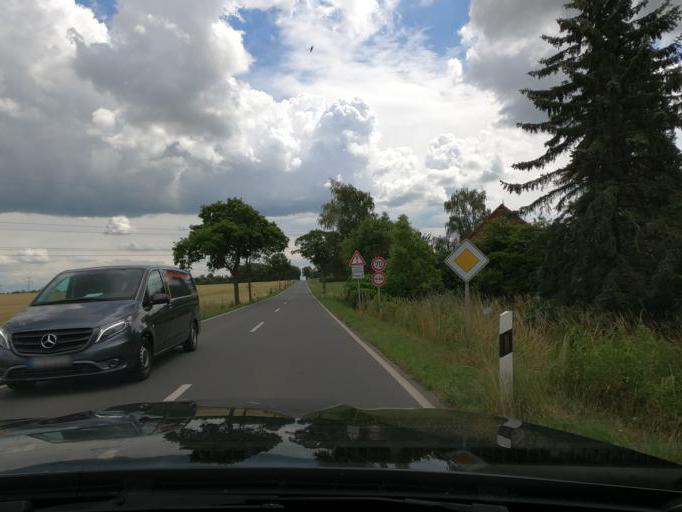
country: DE
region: Lower Saxony
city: Sehnde
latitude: 52.2974
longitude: 9.9898
